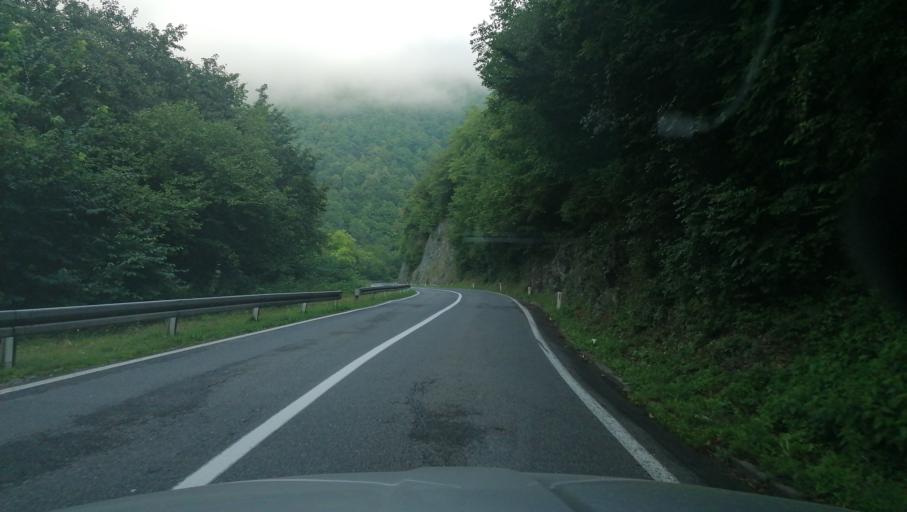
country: BA
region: Federation of Bosnia and Herzegovina
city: Donji Vakuf
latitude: 44.1952
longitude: 17.3363
